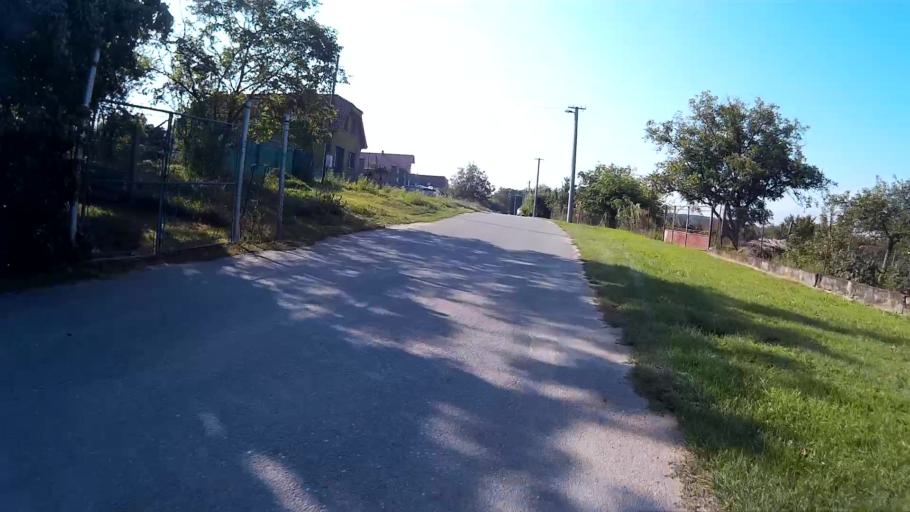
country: CZ
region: South Moravian
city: Vranovice
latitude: 48.9593
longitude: 16.5761
